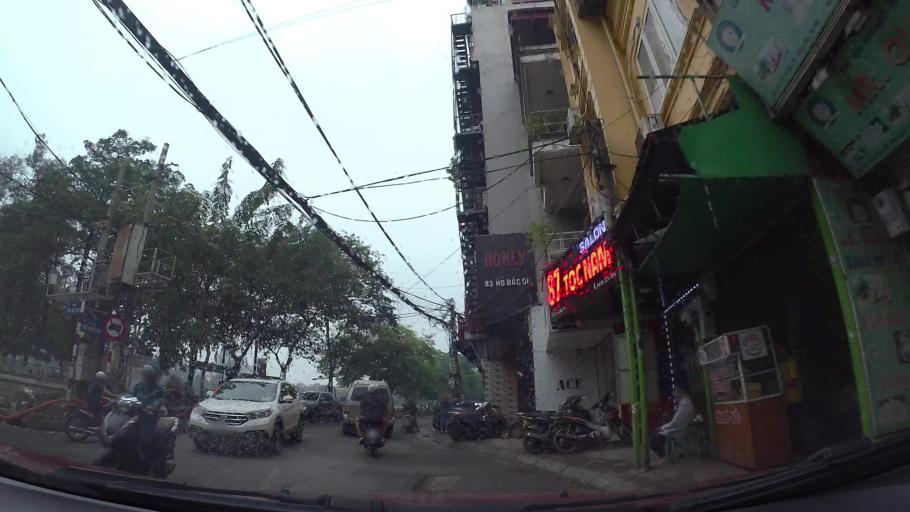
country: VN
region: Ha Noi
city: Dong Da
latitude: 21.0122
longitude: 105.8292
